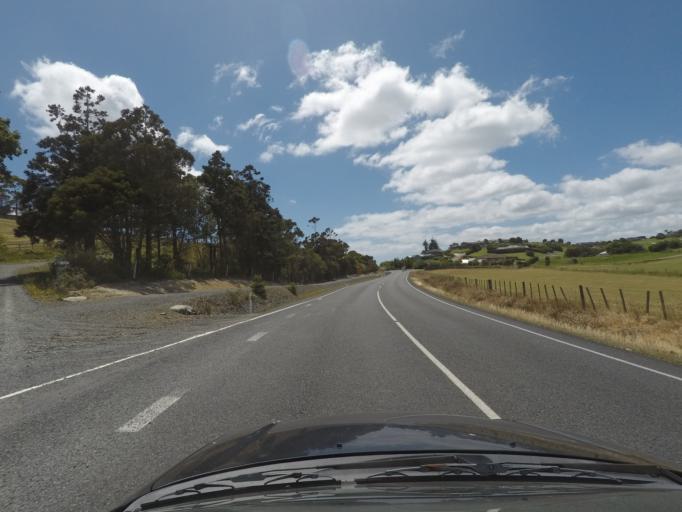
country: NZ
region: Northland
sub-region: Whangarei
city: Ruakaka
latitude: -35.9933
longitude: 174.4655
